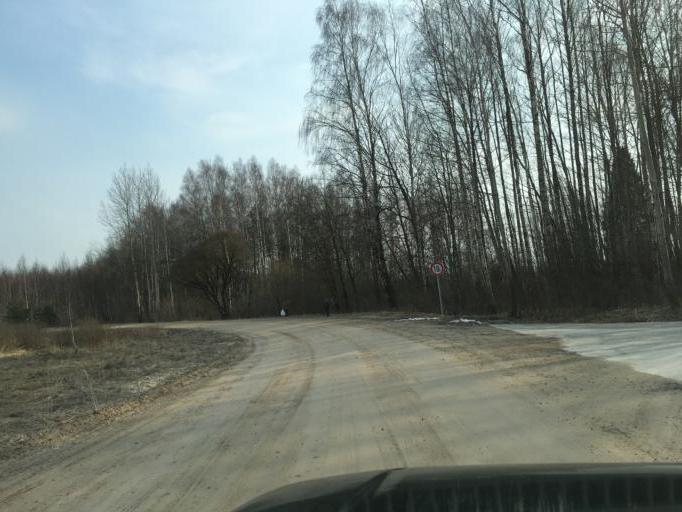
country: LV
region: Olaine
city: Olaine
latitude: 56.7926
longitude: 23.9861
